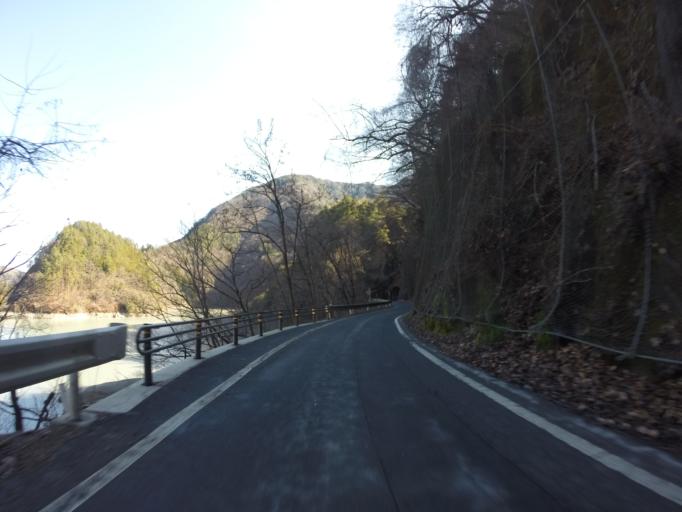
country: JP
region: Yamanashi
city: Ryuo
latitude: 35.4071
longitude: 138.3286
